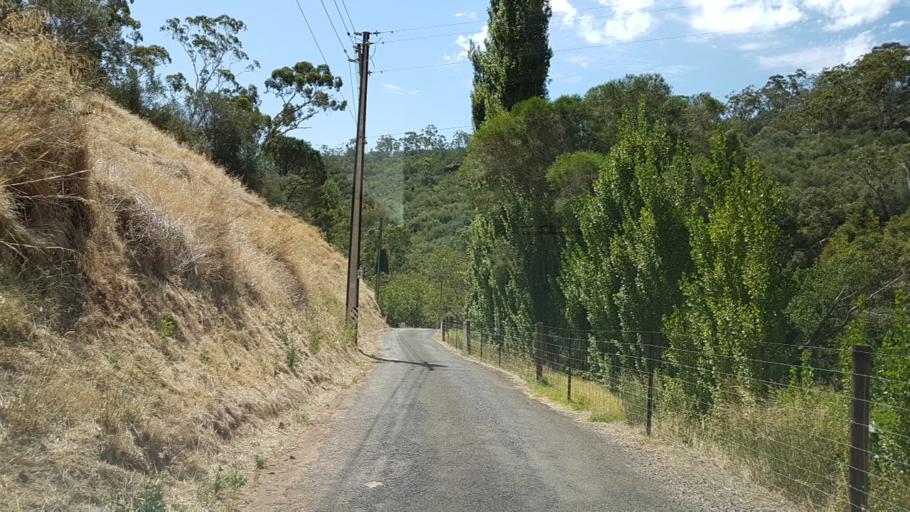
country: AU
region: South Australia
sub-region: Burnside
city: Mount Osmond
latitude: -34.9910
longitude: 138.6544
